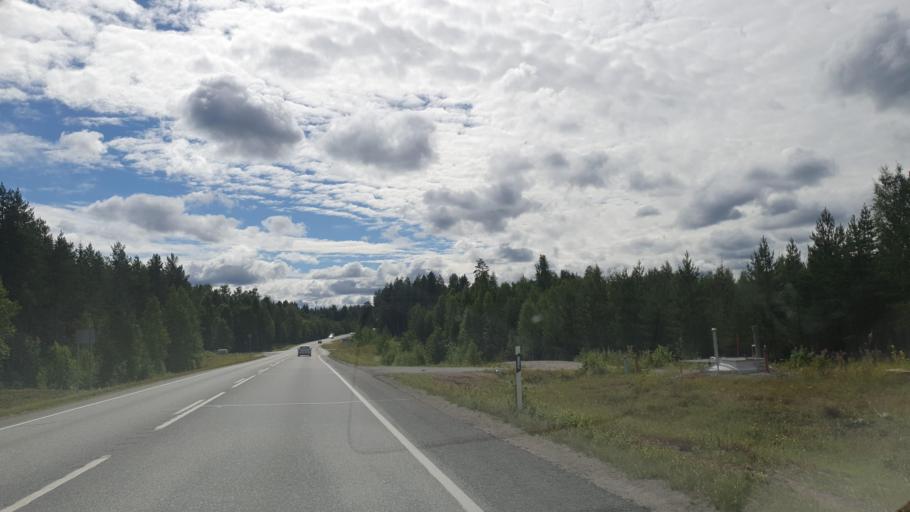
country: FI
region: Kainuu
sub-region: Kajaani
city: Kajaani
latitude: 64.1870
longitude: 27.5997
